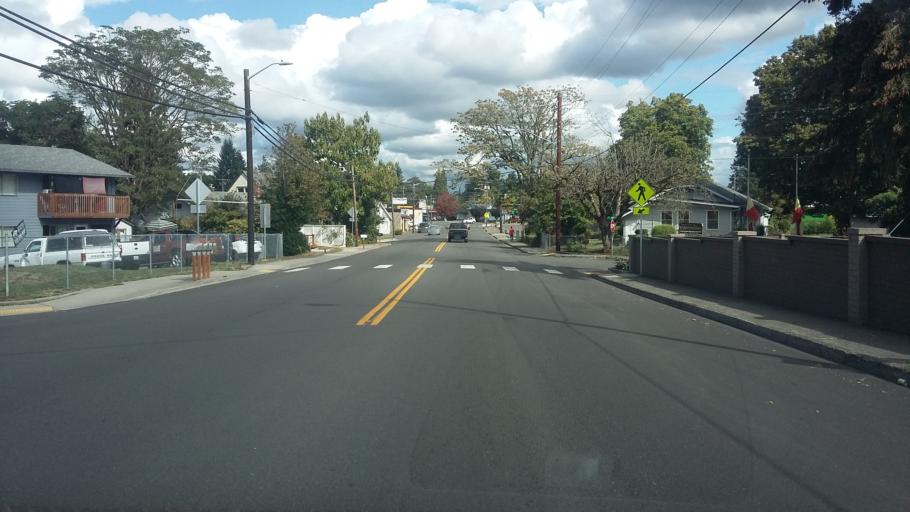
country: US
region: Washington
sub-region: Clark County
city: Vancouver
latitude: 45.6407
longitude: -122.6506
